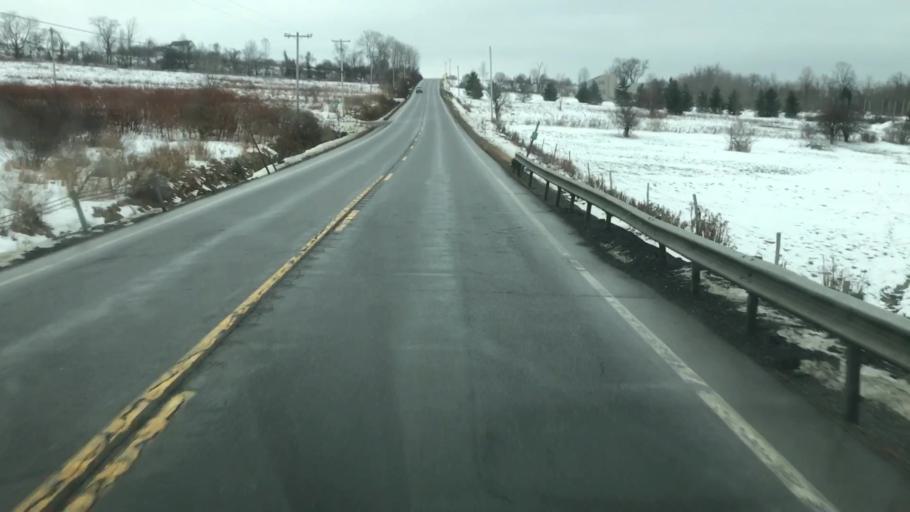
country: US
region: New York
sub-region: Cortland County
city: Cortland West
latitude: 42.6410
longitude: -76.2300
